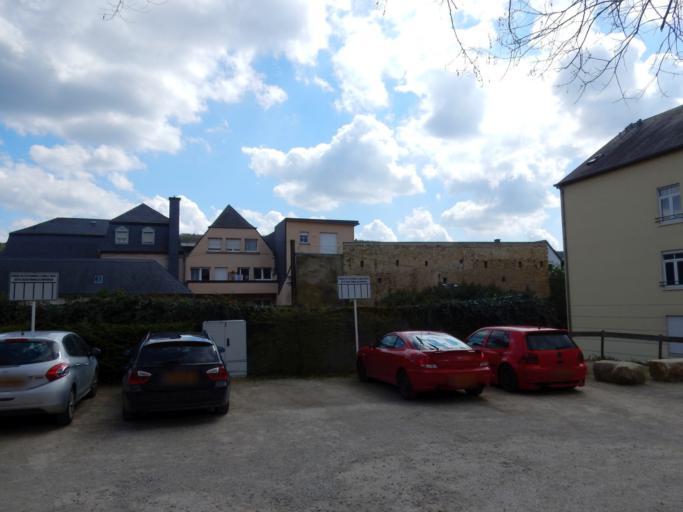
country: LU
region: Grevenmacher
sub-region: Canton de Grevenmacher
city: Grevenmacher
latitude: 49.6794
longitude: 6.4429
